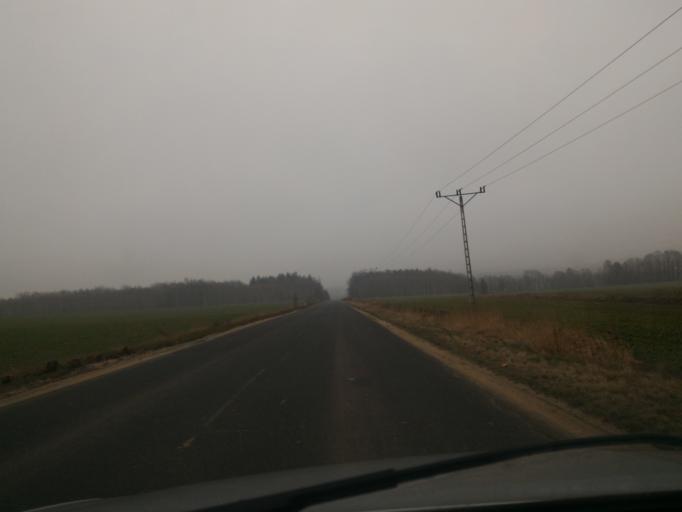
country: PL
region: Lower Silesian Voivodeship
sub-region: Powiat zgorzelecki
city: Bogatynia
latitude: 50.8756
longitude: 14.9074
